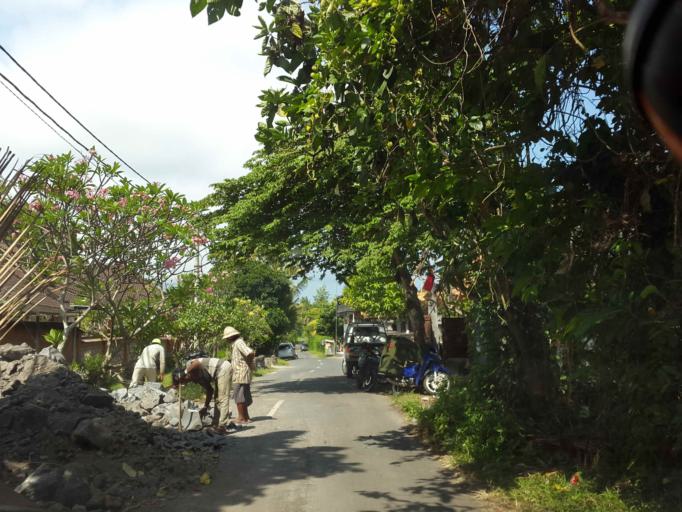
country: ID
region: Bali
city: Klungkung
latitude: -8.5441
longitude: 115.3729
